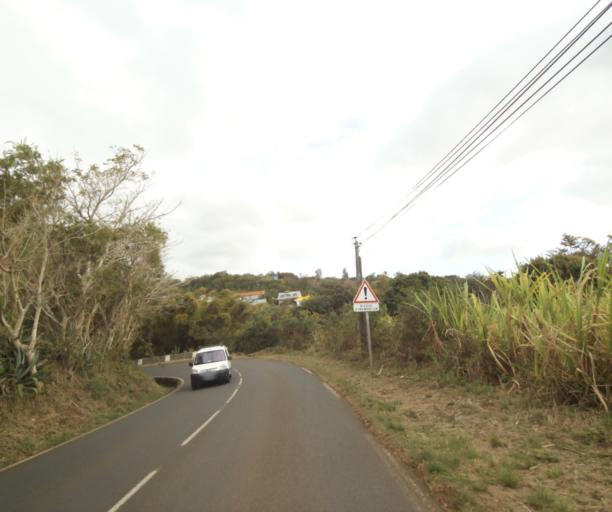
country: RE
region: Reunion
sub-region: Reunion
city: Saint-Paul
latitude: -21.0440
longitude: 55.2879
